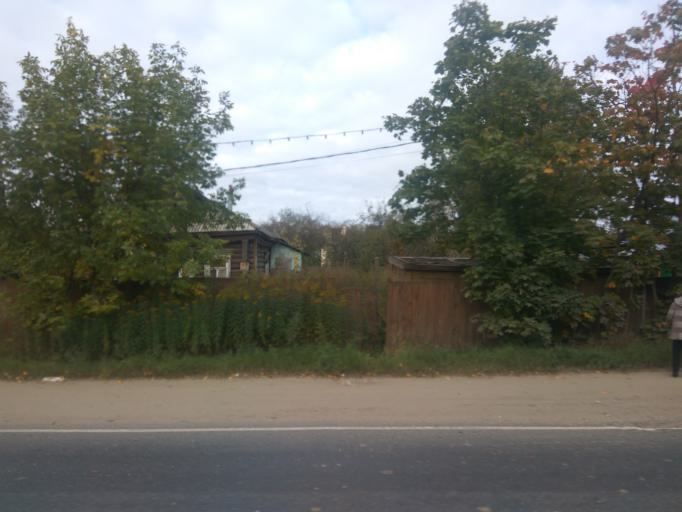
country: RU
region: Moskovskaya
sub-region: Shchelkovskiy Rayon
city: Grebnevo
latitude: 55.9592
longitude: 38.0720
